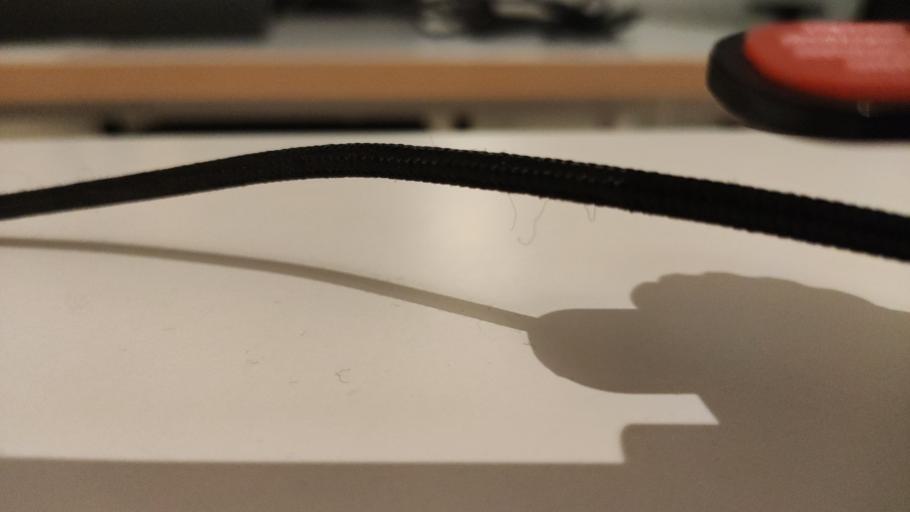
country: RU
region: Moskovskaya
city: Budenovetc
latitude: 56.3782
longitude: 37.5951
